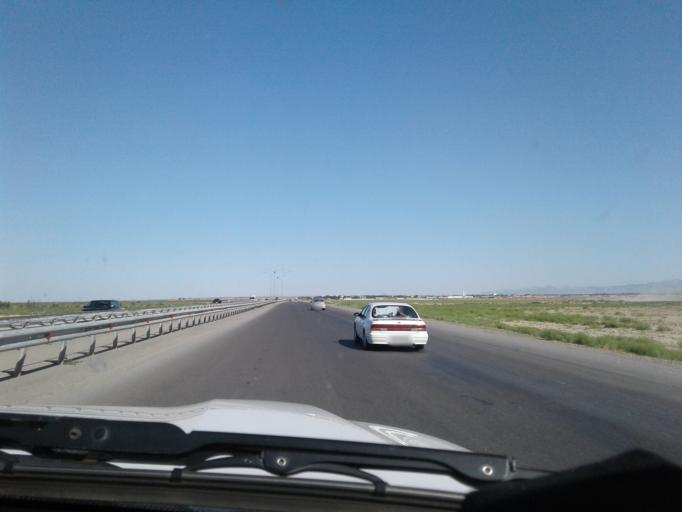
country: TM
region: Ahal
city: Kaka
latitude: 37.3814
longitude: 59.5927
